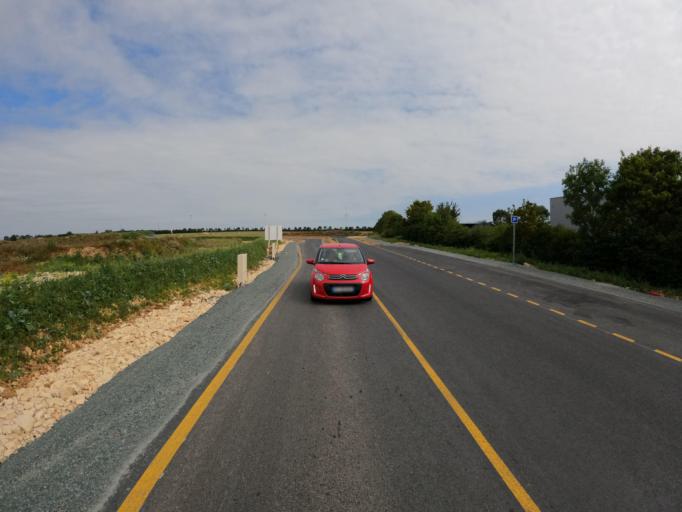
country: FR
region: Poitou-Charentes
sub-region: Departement de la Charente-Maritime
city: Saint-Jean-de-Liversay
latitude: 46.2286
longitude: -0.8760
